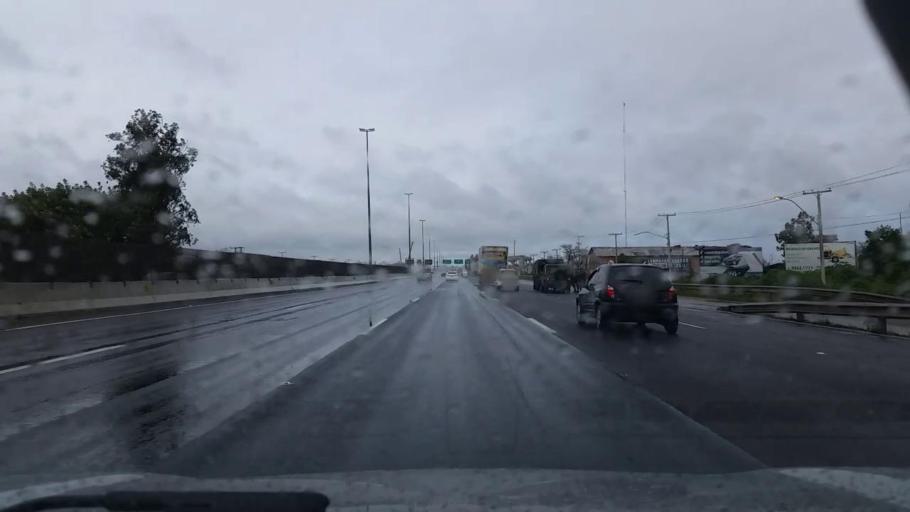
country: BR
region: Rio Grande do Sul
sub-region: Porto Alegre
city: Porto Alegre
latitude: -29.9806
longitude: -51.2011
